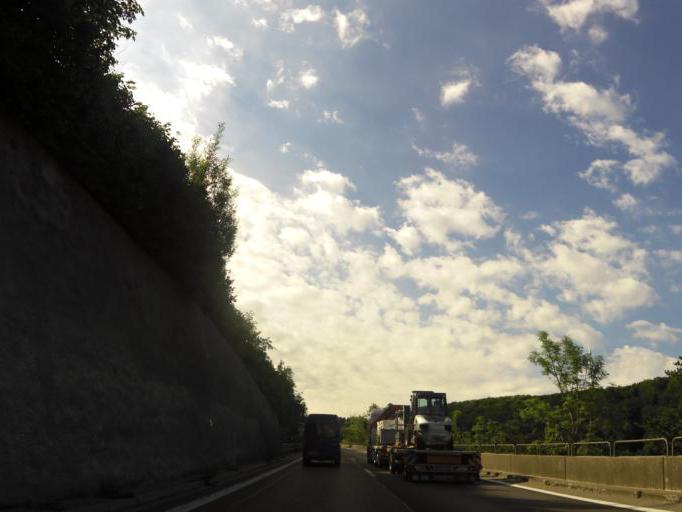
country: DE
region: Baden-Wuerttemberg
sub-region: Regierungsbezirk Stuttgart
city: Wiesensteig
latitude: 48.5577
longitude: 9.6303
